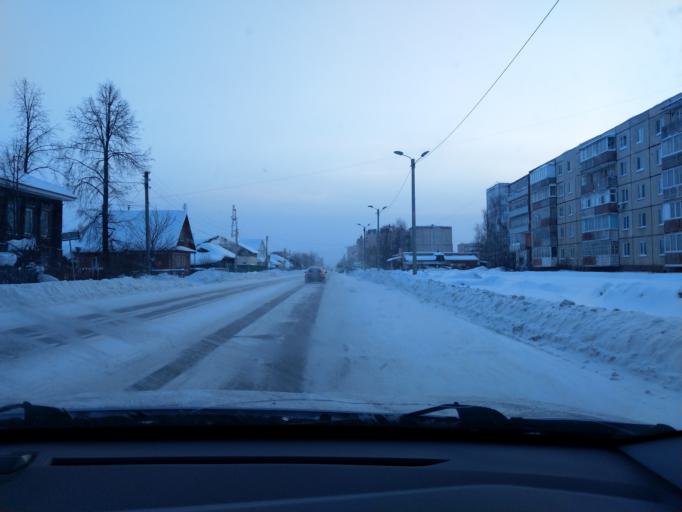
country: RU
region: Perm
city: Dobryanka
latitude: 58.4709
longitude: 56.4064
